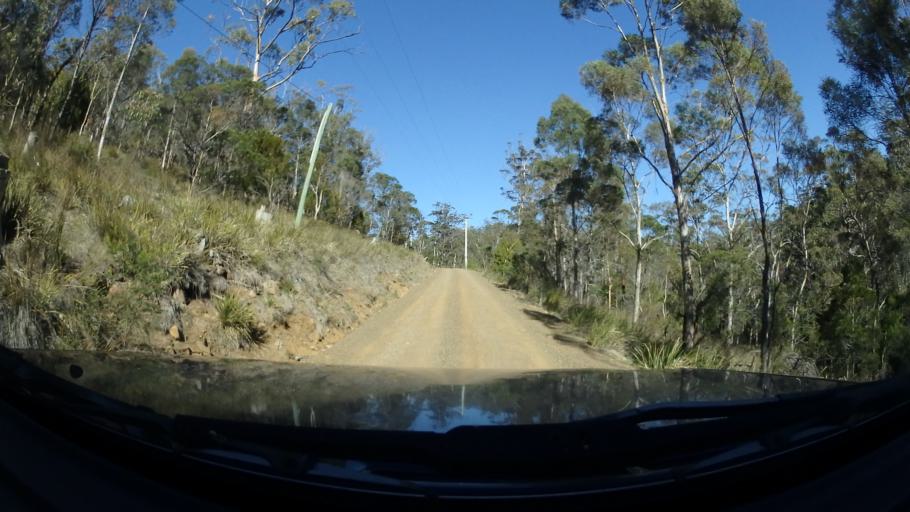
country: AU
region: Tasmania
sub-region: Sorell
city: Sorell
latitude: -42.5376
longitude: 147.8676
